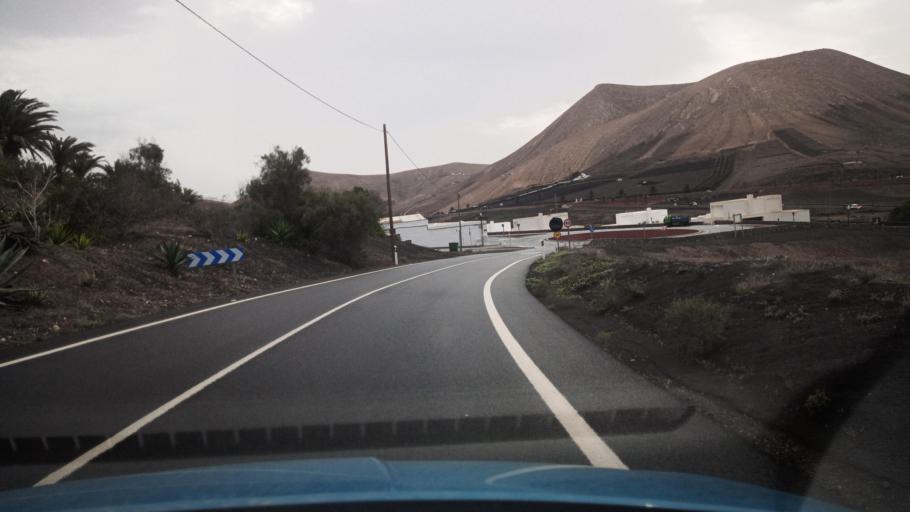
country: ES
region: Canary Islands
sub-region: Provincia de Las Palmas
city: Yaiza
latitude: 28.9484
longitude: -13.7387
